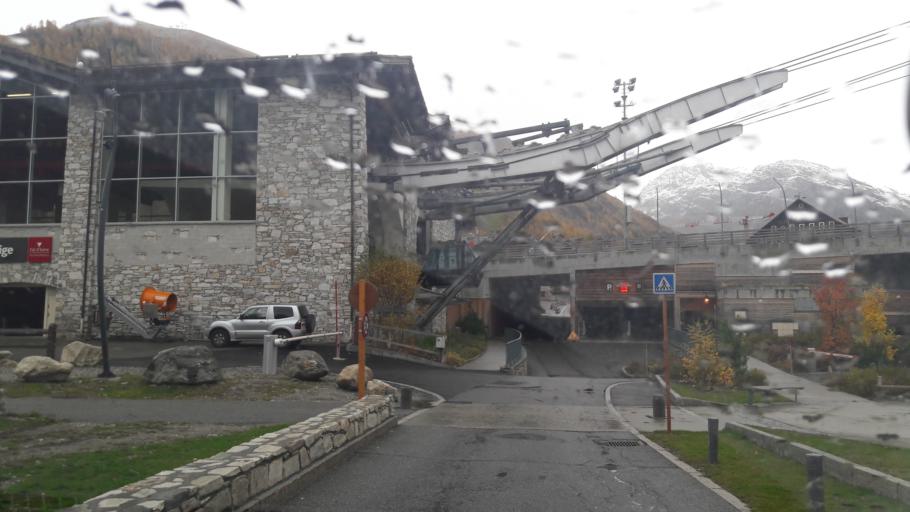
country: FR
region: Rhone-Alpes
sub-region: Departement de la Savoie
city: Val-d'Isere
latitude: 45.4471
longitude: 6.9758
